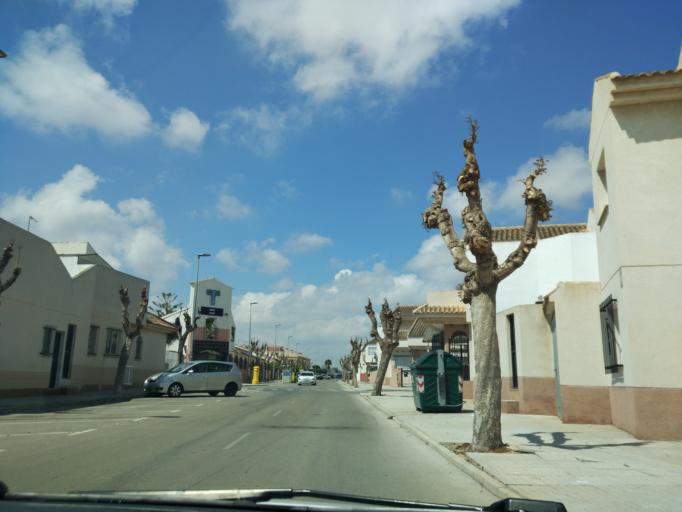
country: ES
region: Murcia
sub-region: Murcia
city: Los Alcazares
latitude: 37.7491
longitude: -0.8512
